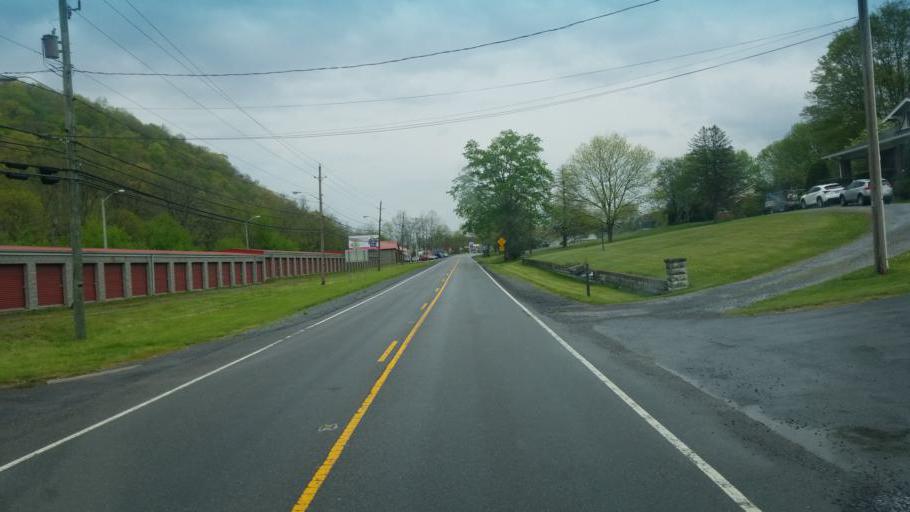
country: US
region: Virginia
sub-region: Smyth County
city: Atkins
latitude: 36.8642
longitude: -81.4392
